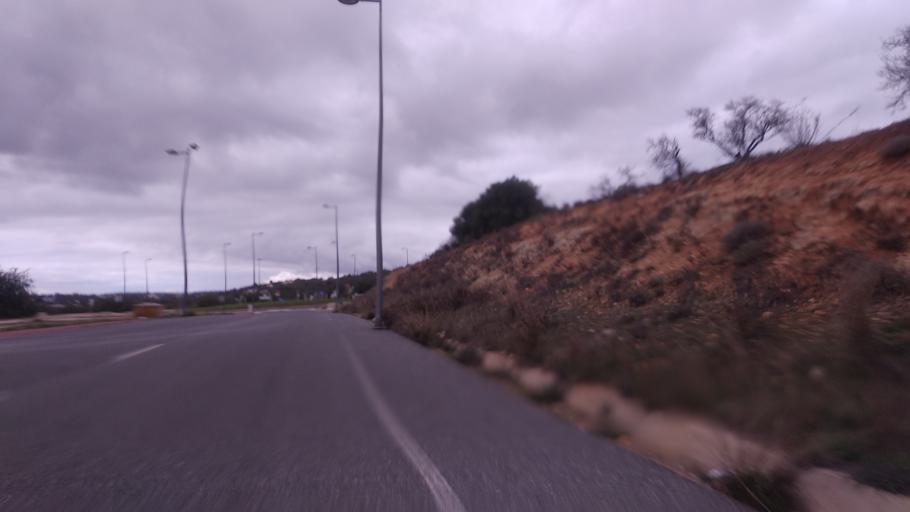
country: PT
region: Faro
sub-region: Faro
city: Santa Barbara de Nexe
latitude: 37.0910
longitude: -7.9765
